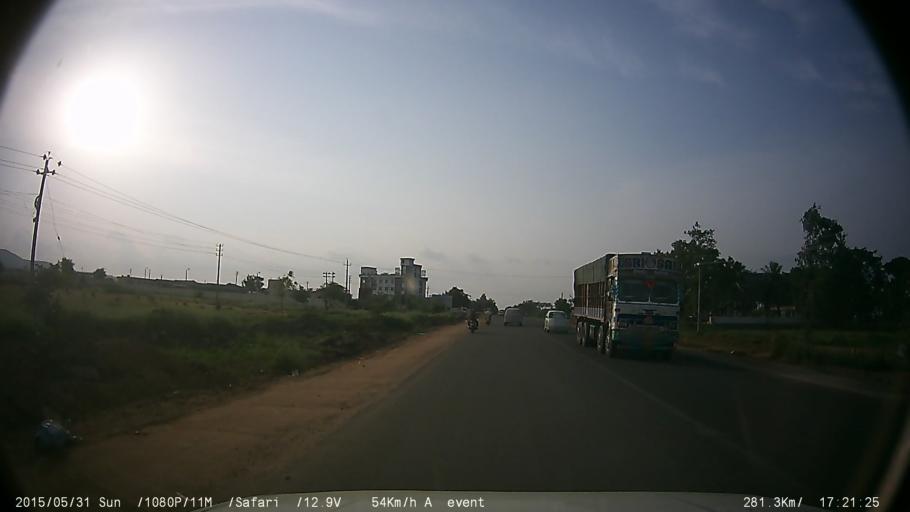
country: IN
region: Karnataka
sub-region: Chamrajnagar
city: Gundlupet
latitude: 11.8275
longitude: 76.6795
